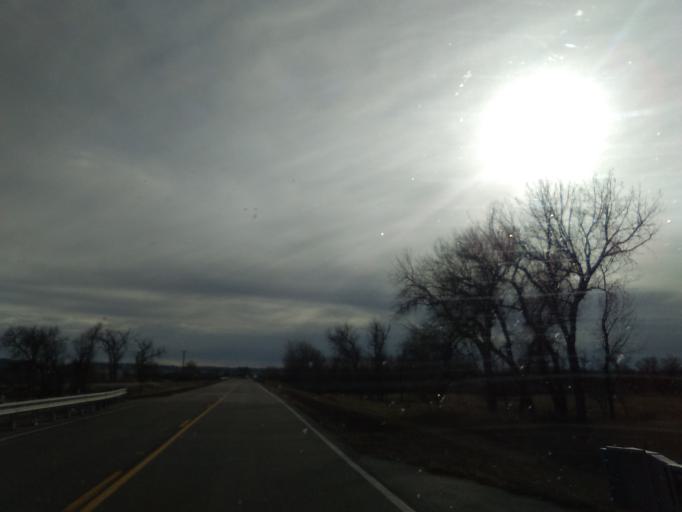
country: US
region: Nebraska
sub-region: Scotts Bluff County
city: Gering
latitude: 41.7920
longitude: -103.5191
